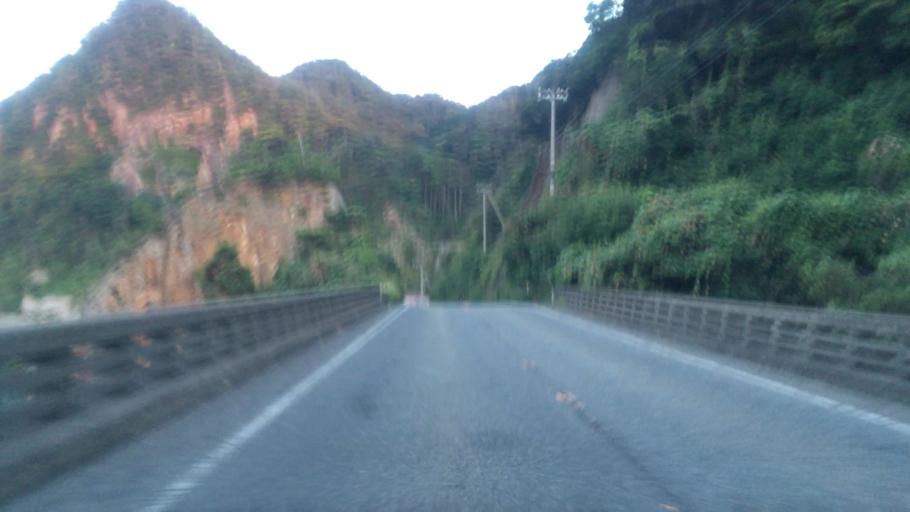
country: JP
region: Tottori
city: Tottori
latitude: 35.6172
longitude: 134.3990
